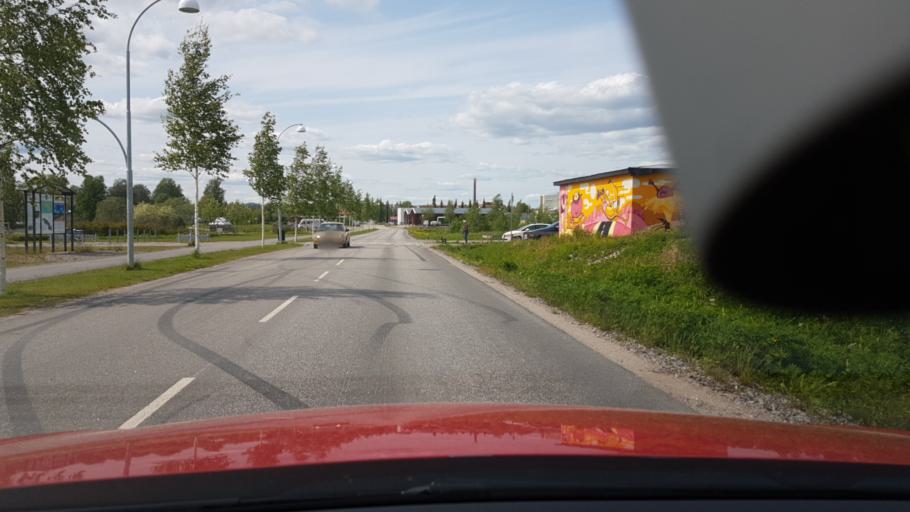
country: SE
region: Gaevleborg
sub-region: Ljusdals Kommun
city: Ljusdal
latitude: 61.8245
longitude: 16.0971
